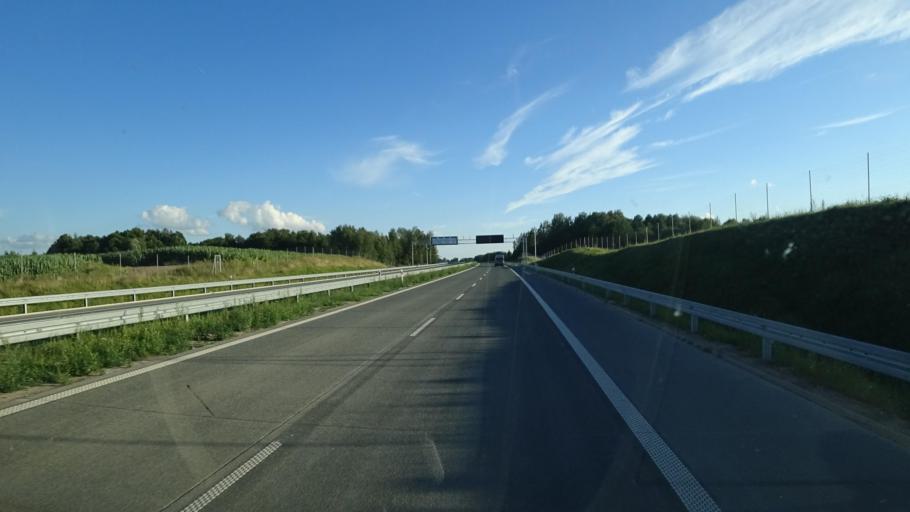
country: PL
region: Podlasie
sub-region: Powiat suwalski
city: Raczki
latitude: 53.9588
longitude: 22.7718
